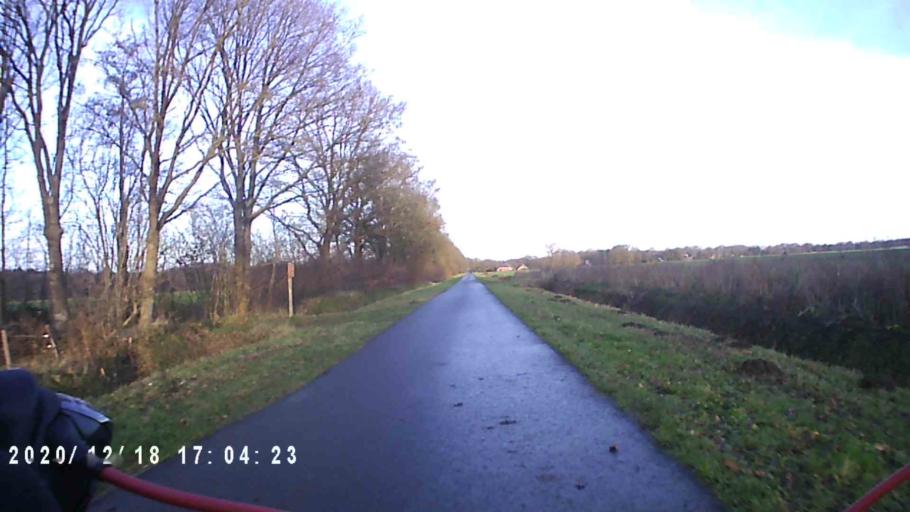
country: NL
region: Drenthe
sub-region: Gemeente Tynaarlo
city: Tynaarlo
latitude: 53.0667
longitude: 6.6319
